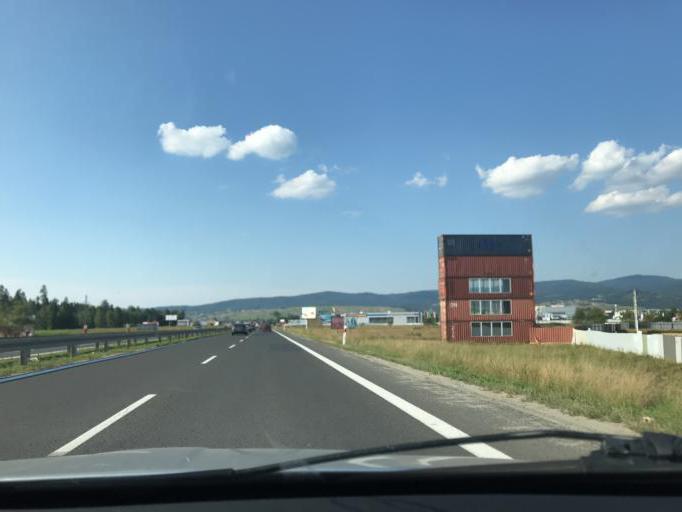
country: PL
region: Lesser Poland Voivodeship
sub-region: Powiat nowotarski
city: Nowy Targ
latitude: 49.4609
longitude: 20.0207
